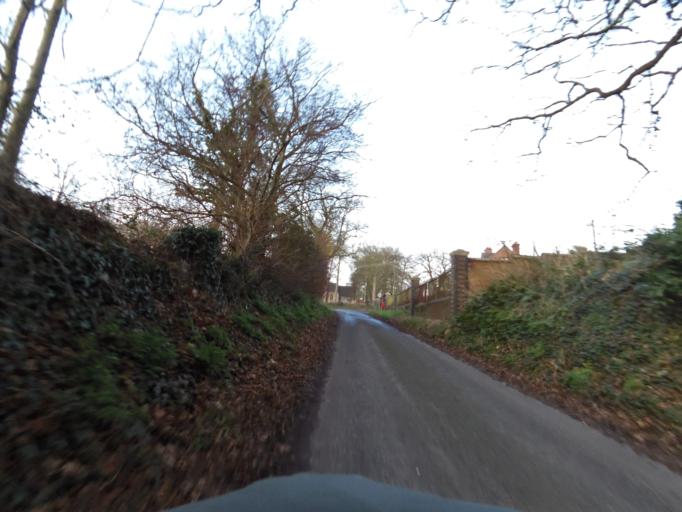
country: GB
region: England
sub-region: Norfolk
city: Sheringham
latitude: 52.8996
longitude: 1.2212
